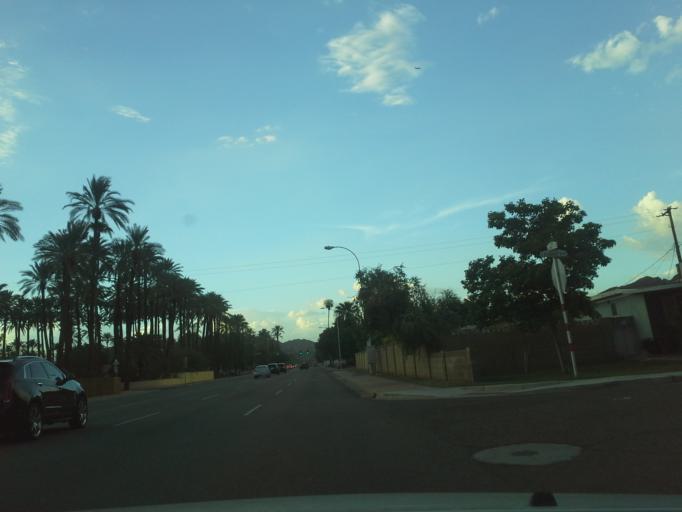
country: US
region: Arizona
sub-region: Maricopa County
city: Paradise Valley
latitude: 33.4998
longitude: -111.9868
